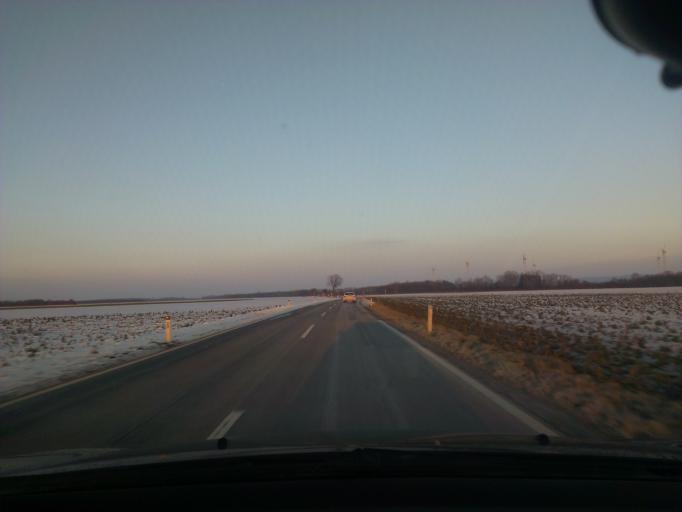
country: AT
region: Lower Austria
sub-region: Politischer Bezirk Baden
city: Mitterndorf an der Fischa
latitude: 47.9622
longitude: 16.4534
